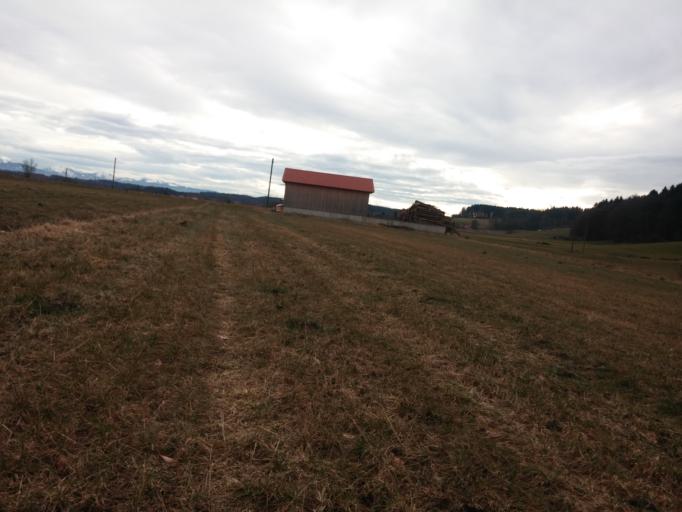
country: DE
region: Bavaria
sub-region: Upper Bavaria
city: Glonn
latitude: 48.0023
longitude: 11.8633
